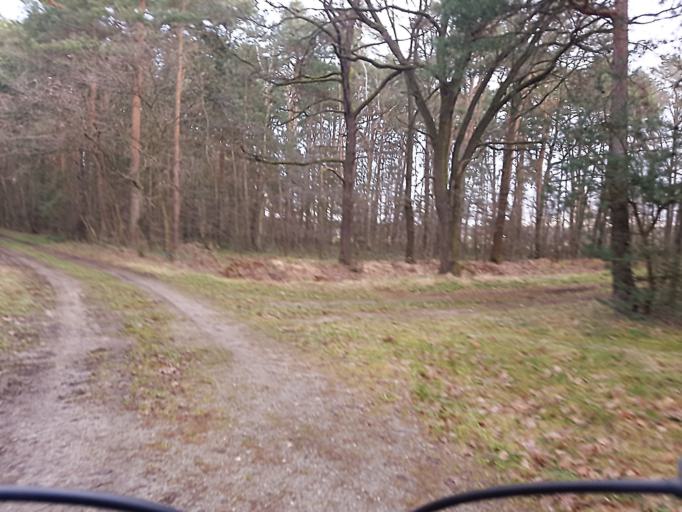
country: DE
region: Brandenburg
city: Schilda
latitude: 51.5760
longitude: 13.3977
